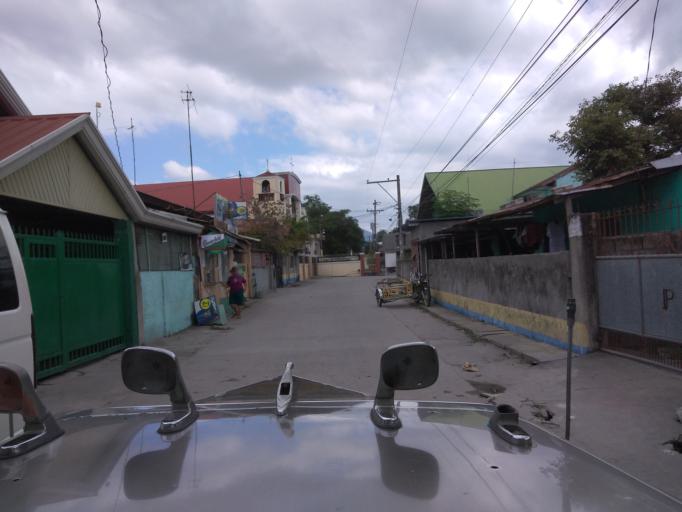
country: PH
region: Central Luzon
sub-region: Province of Pampanga
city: Anao
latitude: 15.1188
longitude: 120.6985
